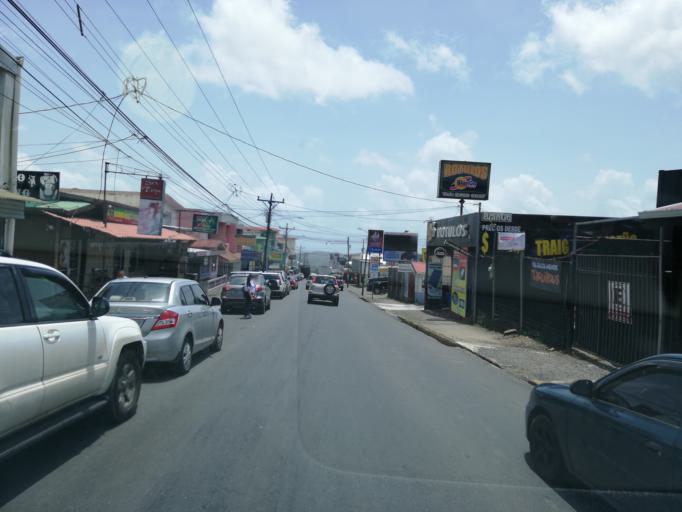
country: CR
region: Alajuela
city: Quesada
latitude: 10.3213
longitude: -84.4296
